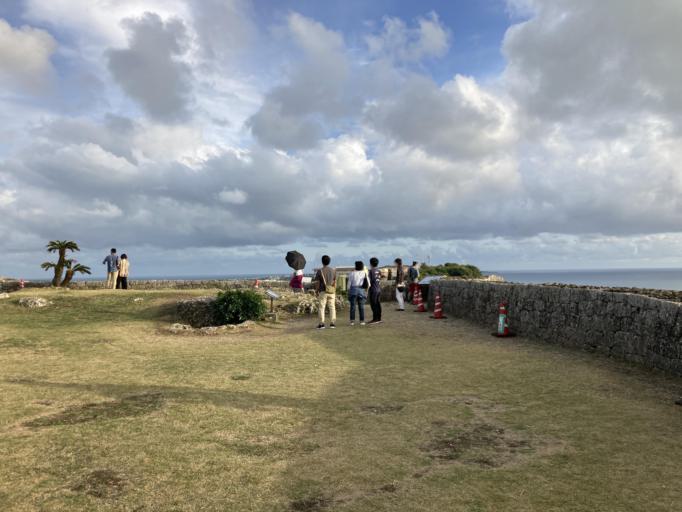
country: JP
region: Okinawa
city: Katsuren-haebaru
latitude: 26.3309
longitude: 127.8785
